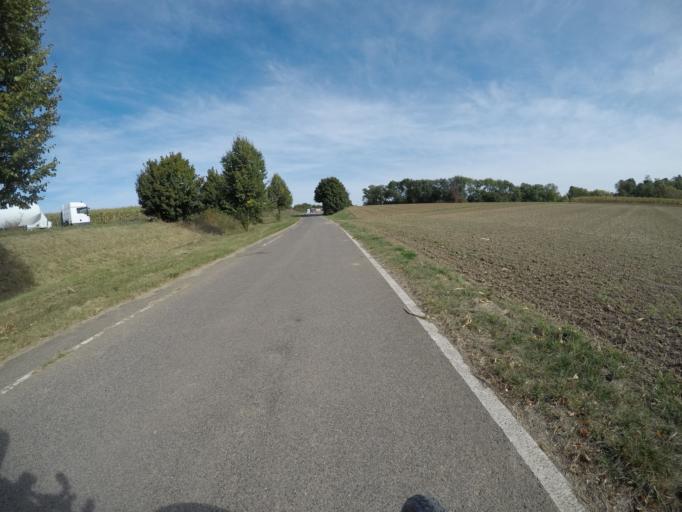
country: DE
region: Baden-Wuerttemberg
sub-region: Regierungsbezirk Stuttgart
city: Schwieberdingen
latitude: 48.8628
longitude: 9.0959
